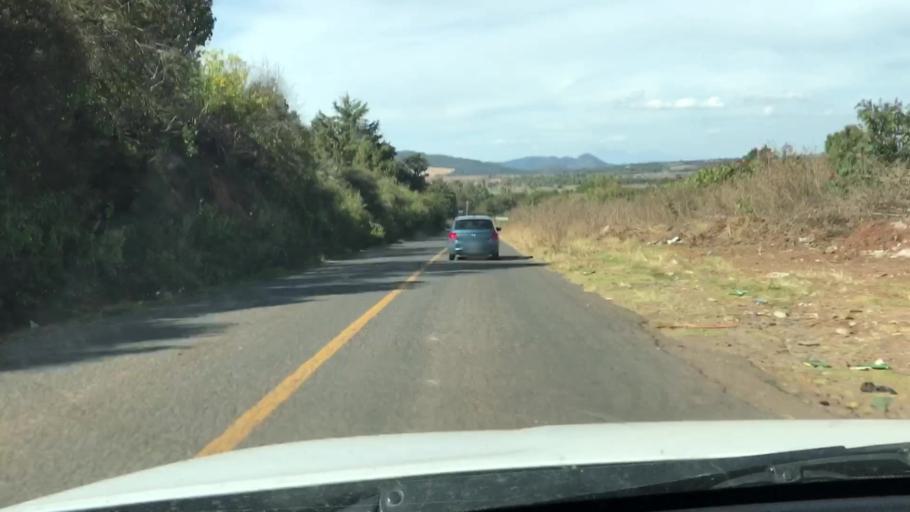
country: MX
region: Jalisco
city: Chiquilistlan
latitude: 20.1450
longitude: -103.7235
